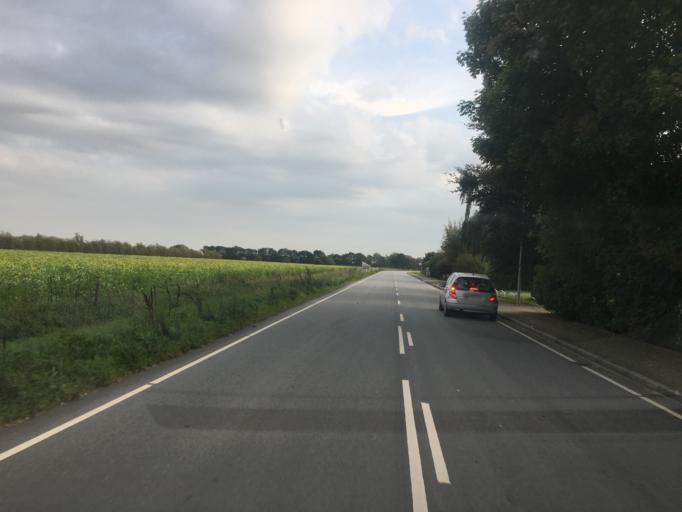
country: DE
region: Schleswig-Holstein
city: Bramstedtlund
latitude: 54.9230
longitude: 9.0700
